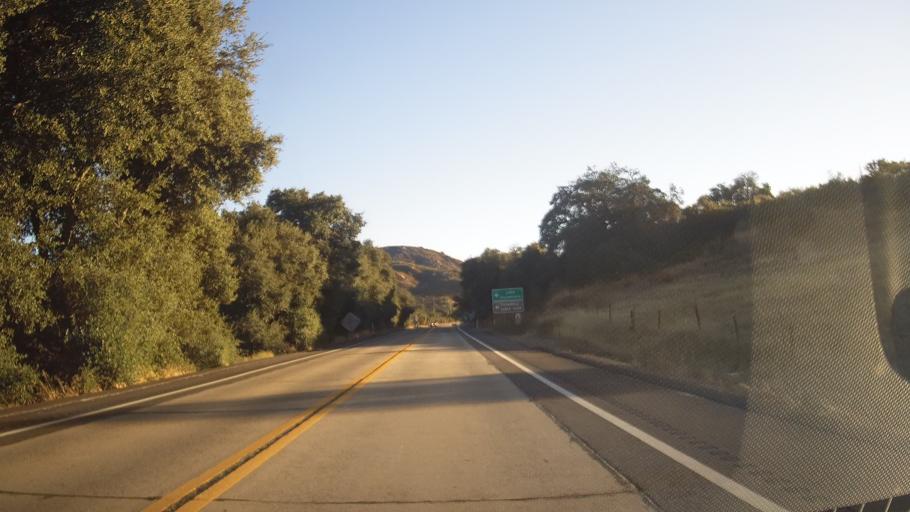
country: US
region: California
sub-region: San Diego County
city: Descanso
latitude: 32.8503
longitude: -116.5963
